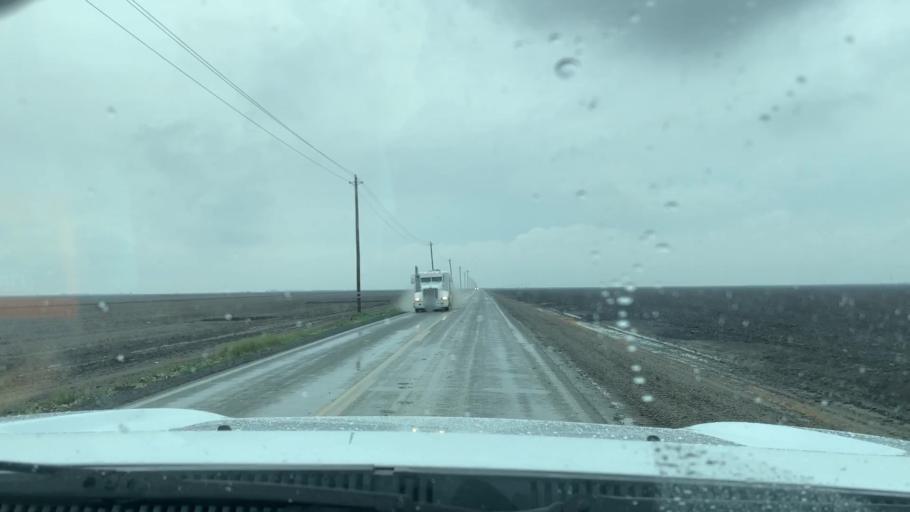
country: US
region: California
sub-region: Kings County
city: Corcoran
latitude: 35.9775
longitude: -119.5720
